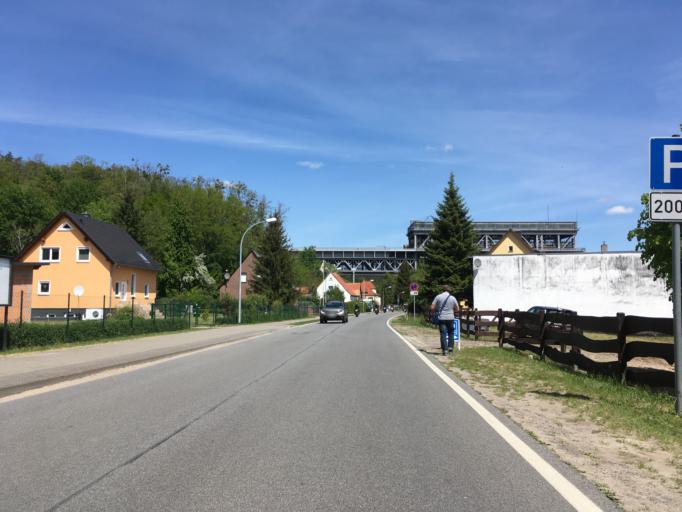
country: DE
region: Brandenburg
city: Niederfinow
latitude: 52.8463
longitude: 13.9391
